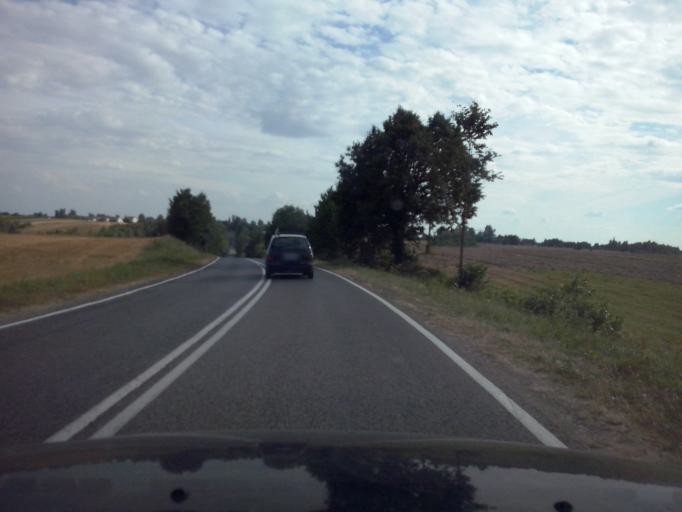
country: PL
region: Swietokrzyskie
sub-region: Powiat kielecki
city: Lagow
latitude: 50.7479
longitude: 21.0713
